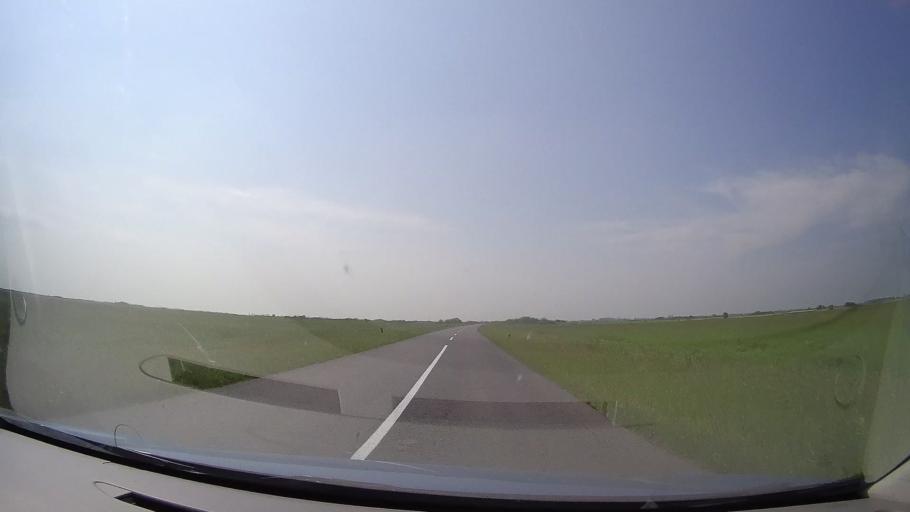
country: RS
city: Jarkovac
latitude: 45.2991
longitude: 20.7627
